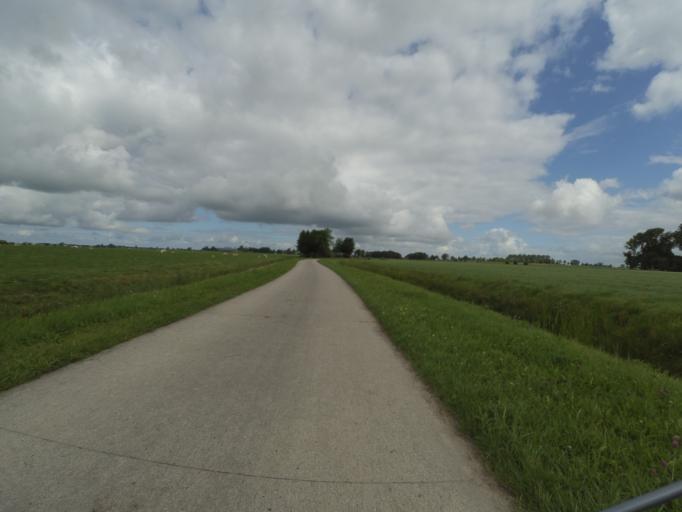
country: NL
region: Friesland
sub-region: Gemeente Kollumerland en Nieuwkruisland
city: Kollum
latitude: 53.2878
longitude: 6.2272
